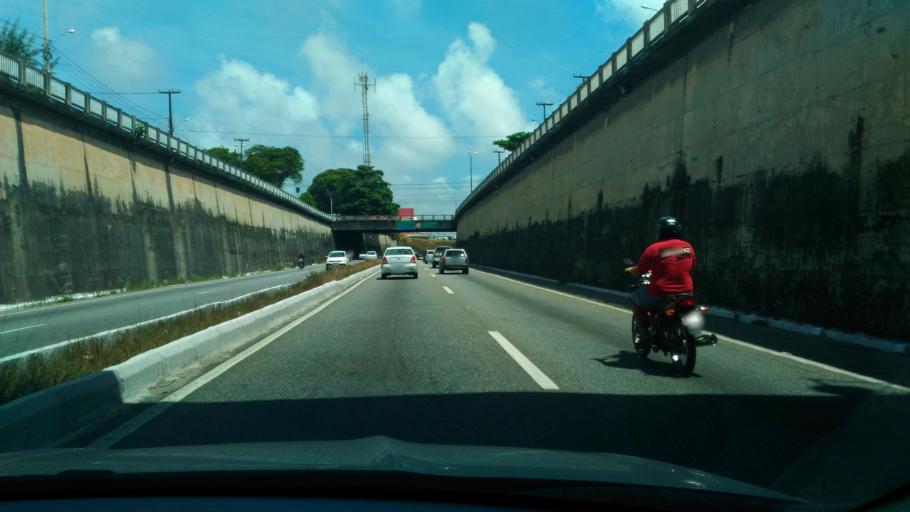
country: BR
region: Paraiba
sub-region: Joao Pessoa
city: Joao Pessoa
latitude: -7.1210
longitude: -34.8452
